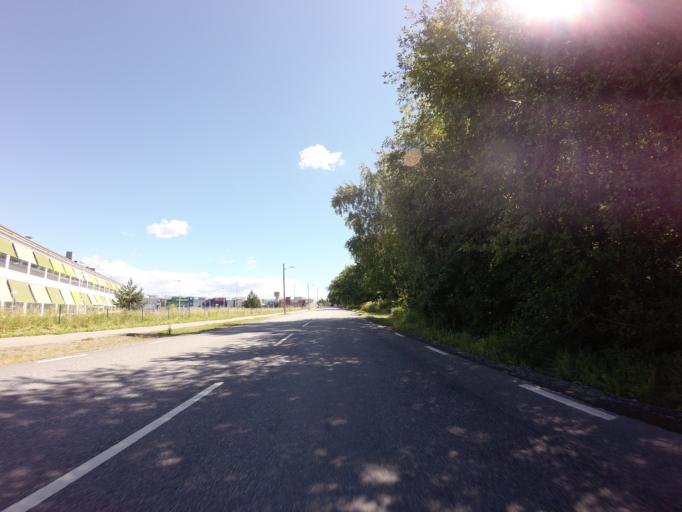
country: SE
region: Stockholm
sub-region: Lidingo
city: Lidingoe
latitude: 59.3394
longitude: 18.1213
